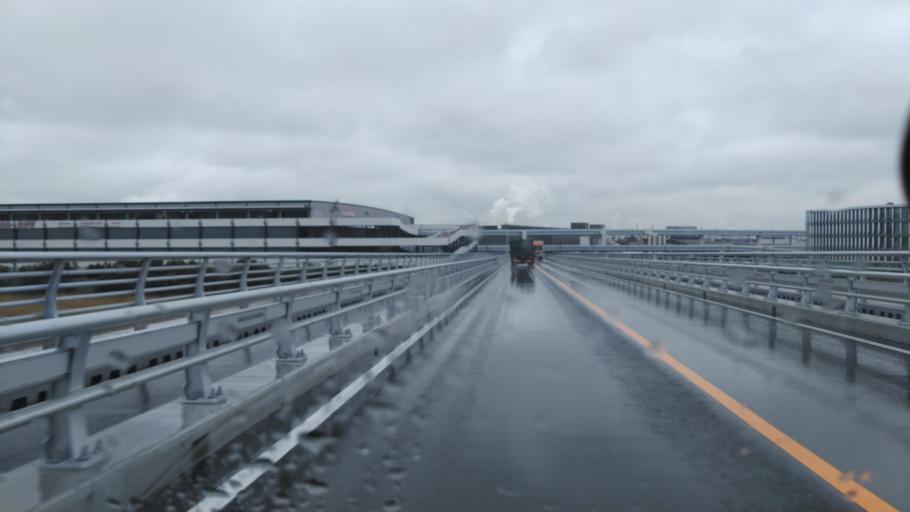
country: JP
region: Kanagawa
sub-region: Kawasaki-shi
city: Kawasaki
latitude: 35.5414
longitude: 139.7616
